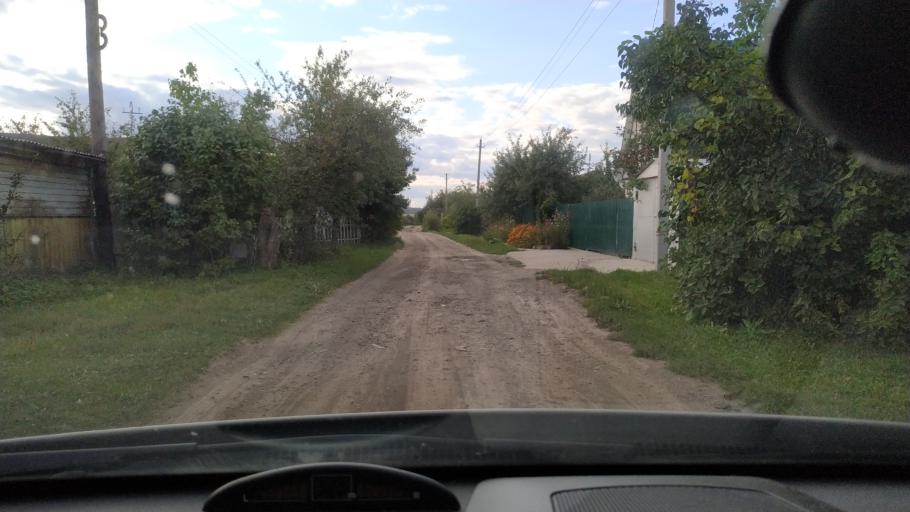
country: RU
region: Rjazan
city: Polyany
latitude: 54.5557
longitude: 39.8740
